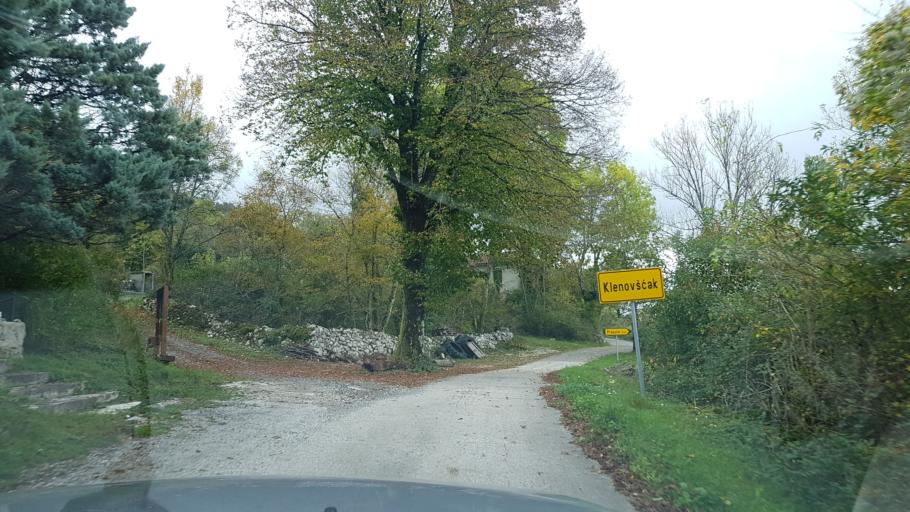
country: HR
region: Istarska
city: Buzet
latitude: 45.4426
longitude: 14.0473
